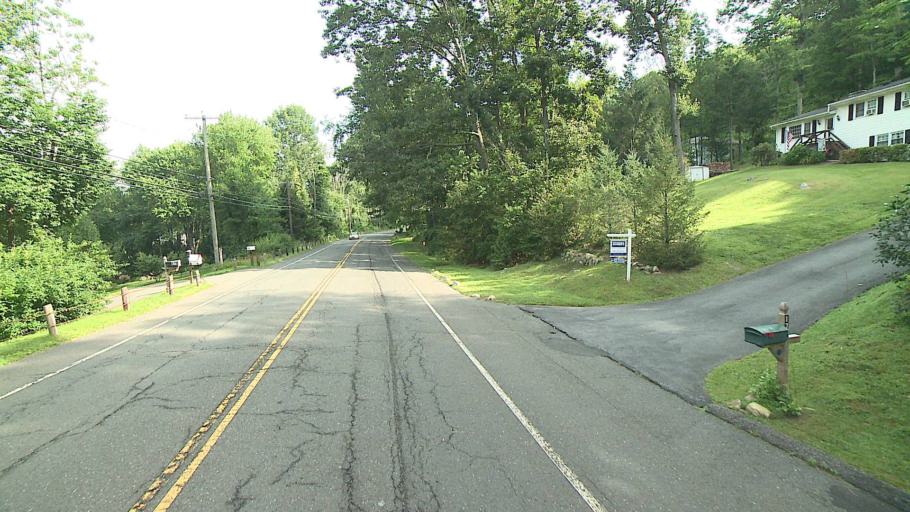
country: US
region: New York
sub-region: Putnam County
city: Putnam Lake
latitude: 41.4761
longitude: -73.4977
